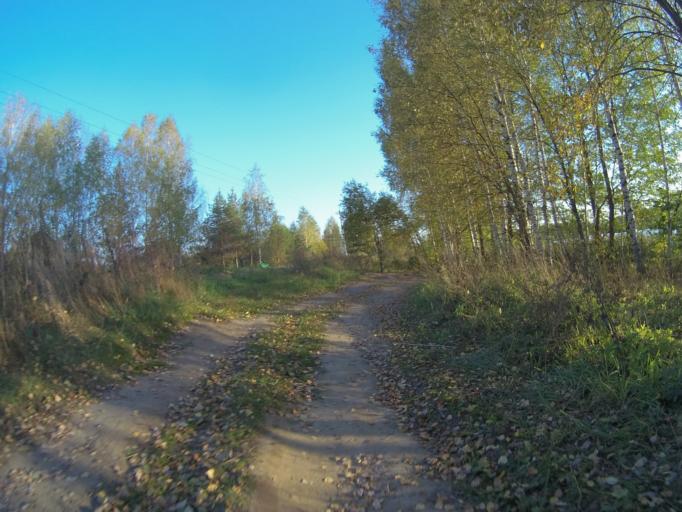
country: RU
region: Vladimir
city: Golovino
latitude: 55.9720
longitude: 40.4564
